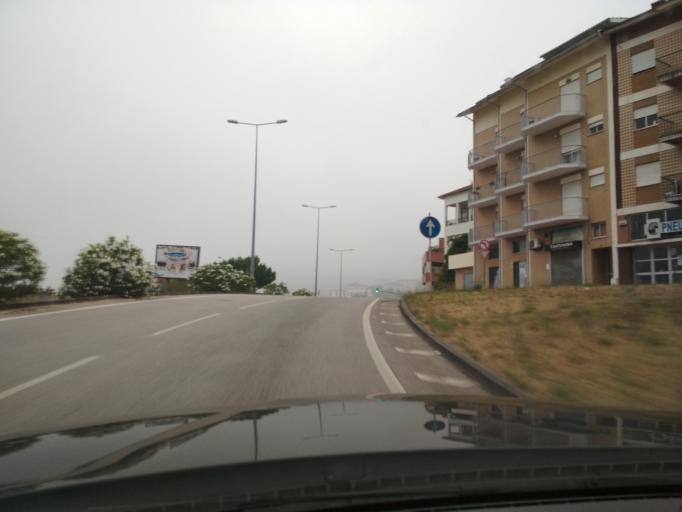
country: PT
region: Coimbra
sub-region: Coimbra
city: Coimbra
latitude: 40.1938
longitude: -8.4207
